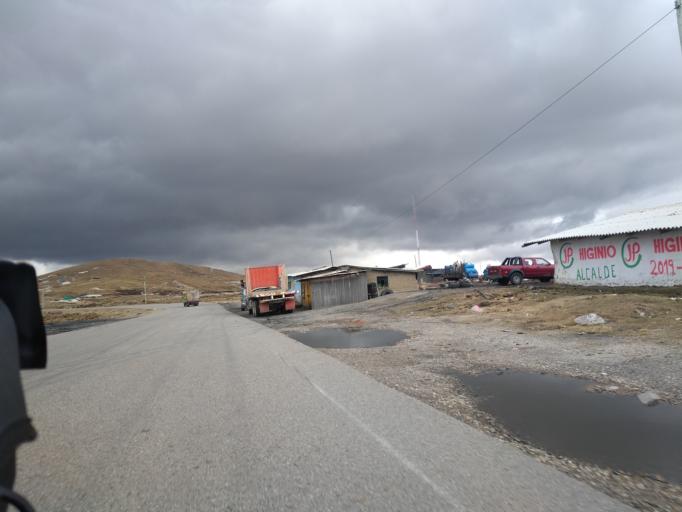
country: PE
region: La Libertad
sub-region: Provincia de Santiago de Chuco
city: Quiruvilca
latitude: -7.9906
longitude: -78.2905
